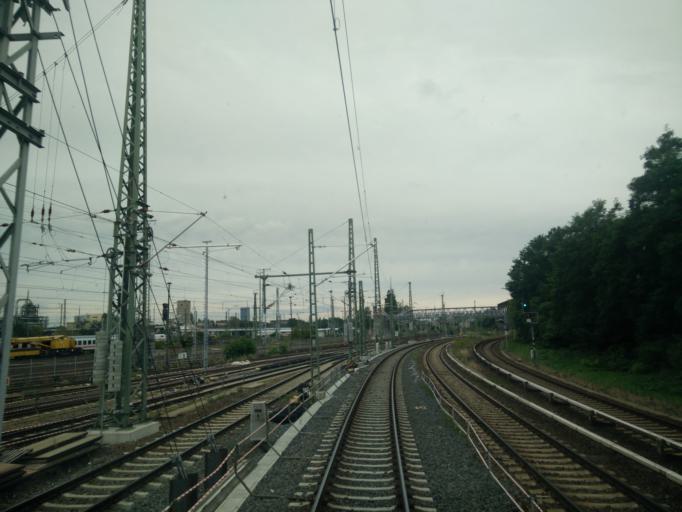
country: DE
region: Berlin
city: Rummelsburg
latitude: 52.4921
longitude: 13.5014
